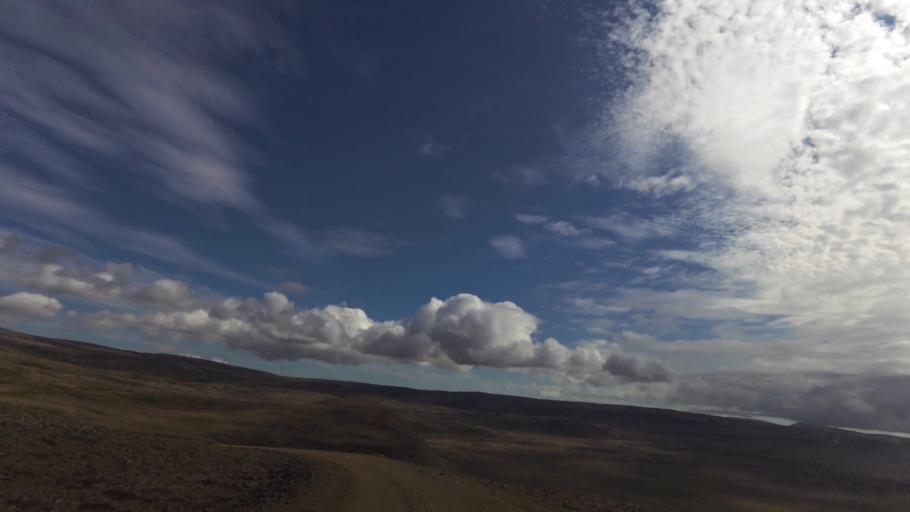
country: IS
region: West
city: Olafsvik
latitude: 65.6194
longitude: -24.3158
